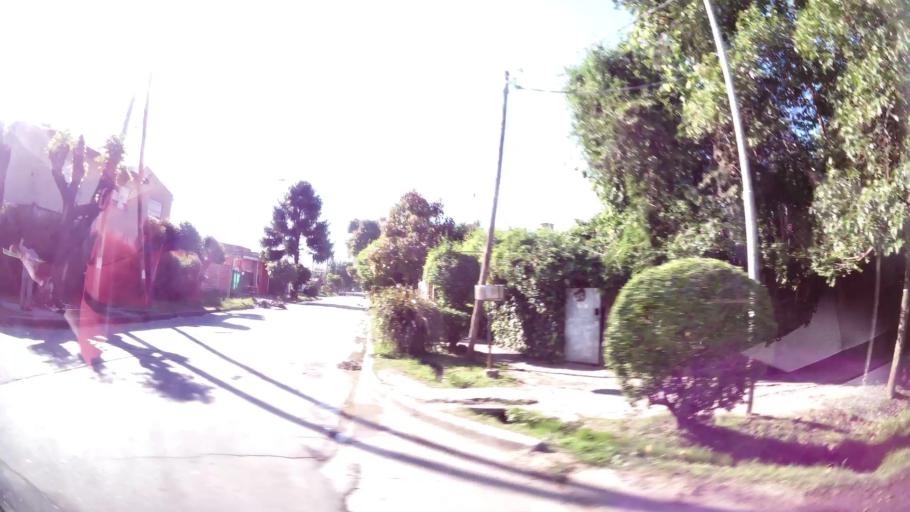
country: AR
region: Buenos Aires
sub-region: Partido de Tigre
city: Tigre
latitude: -34.4868
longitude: -58.6574
